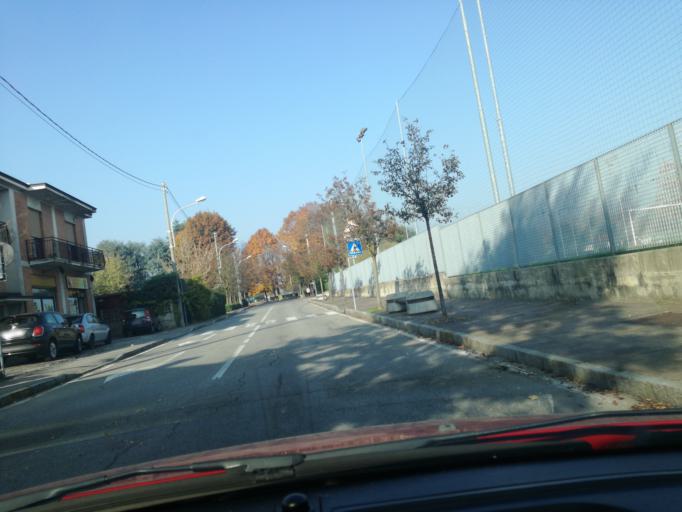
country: IT
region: Lombardy
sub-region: Provincia di Monza e Brianza
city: Cavenago di Brianza
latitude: 45.5878
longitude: 9.4155
